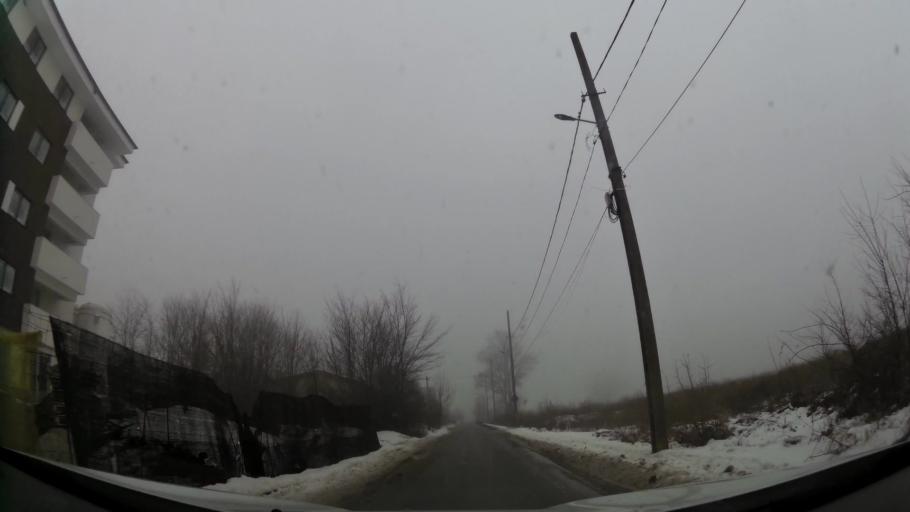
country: RO
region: Ilfov
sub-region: Comuna Chiajna
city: Chiajna
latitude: 44.4587
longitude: 25.9916
